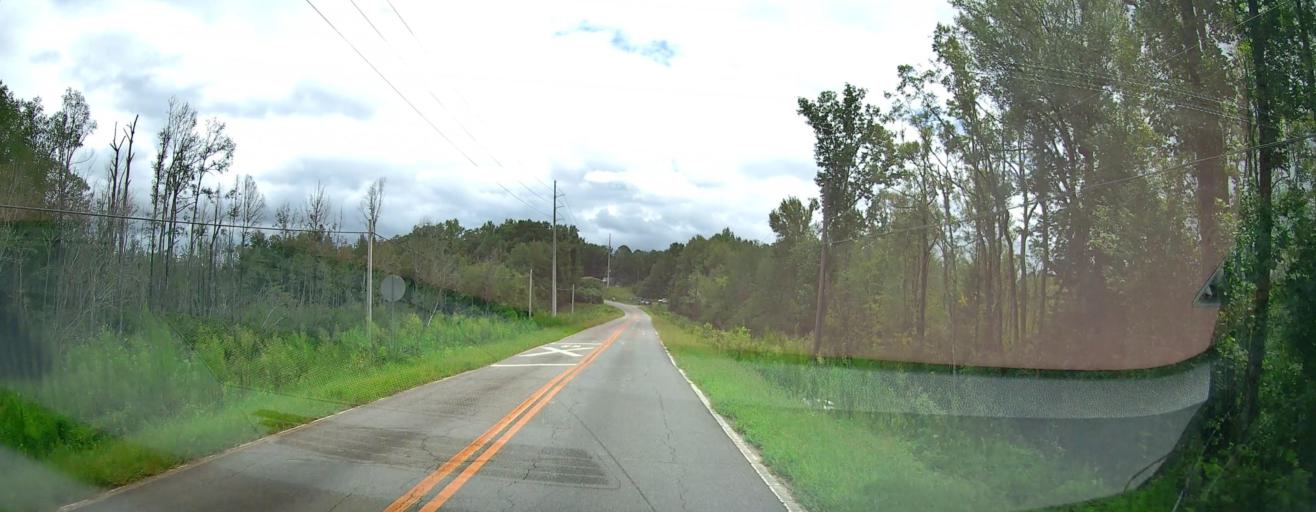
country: US
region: Georgia
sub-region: Bibb County
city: Macon
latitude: 32.8020
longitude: -83.5337
